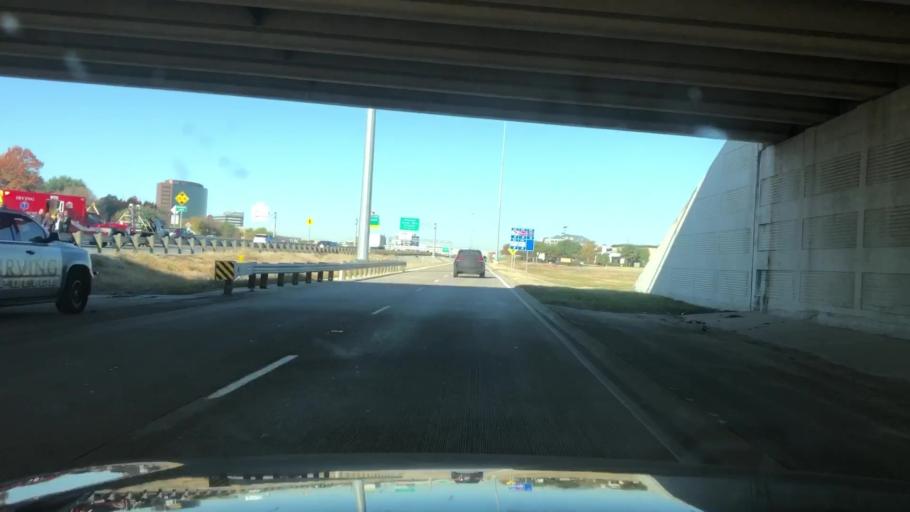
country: US
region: Texas
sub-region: Dallas County
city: Farmers Branch
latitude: 32.8871
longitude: -96.9558
